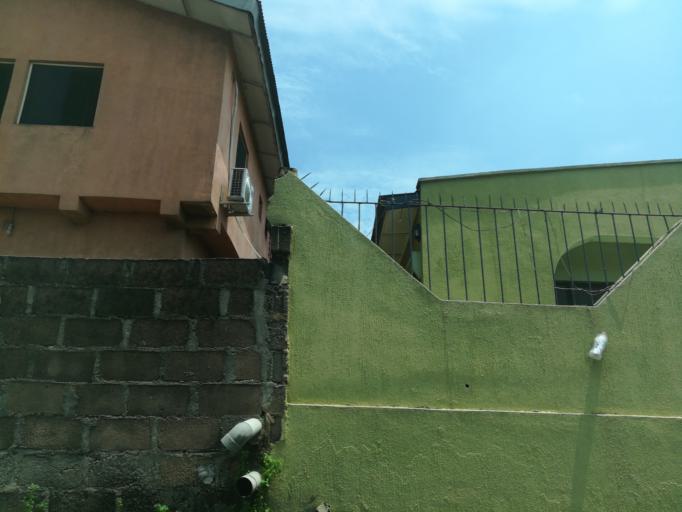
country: NG
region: Lagos
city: Ikorodu
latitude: 6.6226
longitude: 3.4918
